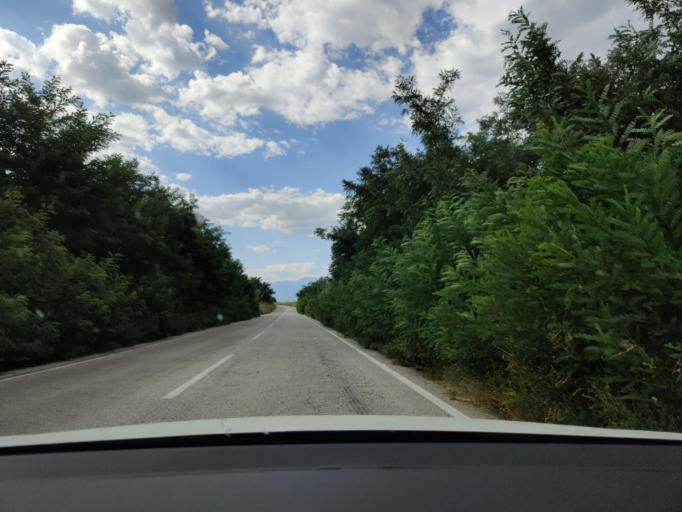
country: GR
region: Central Macedonia
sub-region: Nomos Serron
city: Strymoniko
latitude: 41.0603
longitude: 23.3112
